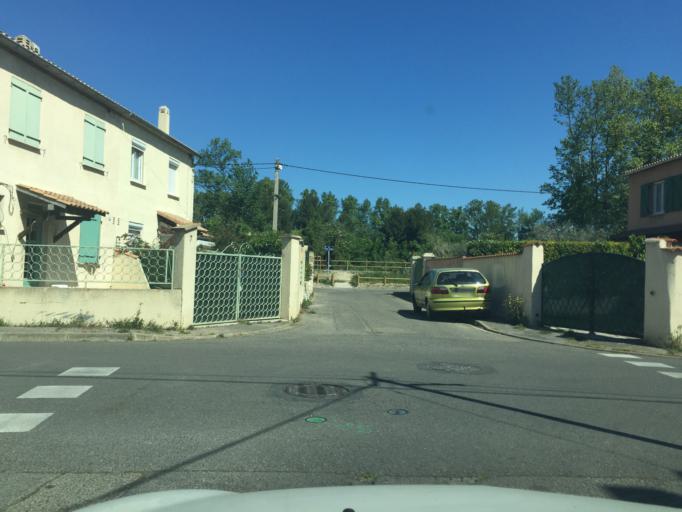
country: FR
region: Provence-Alpes-Cote d'Azur
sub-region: Departement du Vaucluse
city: Le Pontet
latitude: 43.9446
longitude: 4.8380
